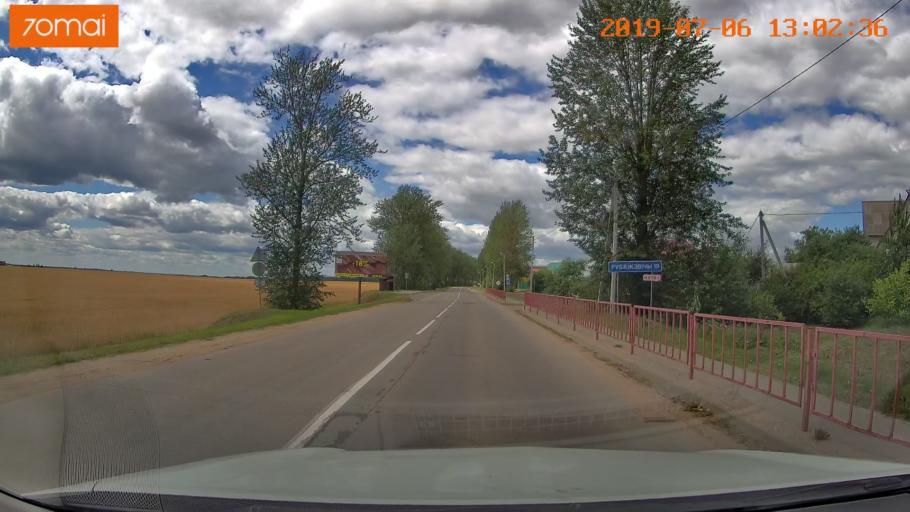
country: BY
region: Minsk
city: Dzyarzhynsk
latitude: 53.6868
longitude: 27.1146
